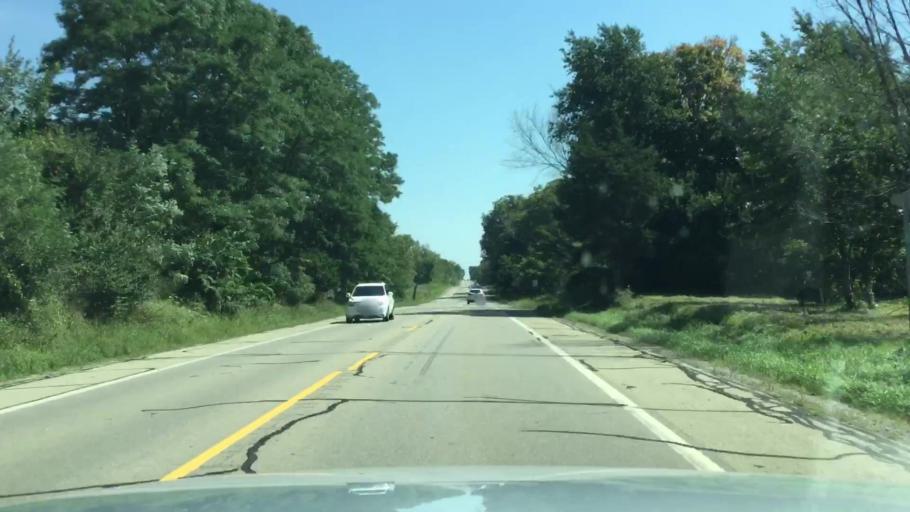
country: US
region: Michigan
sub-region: Washtenaw County
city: Manchester
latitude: 42.0726
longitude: -84.0618
